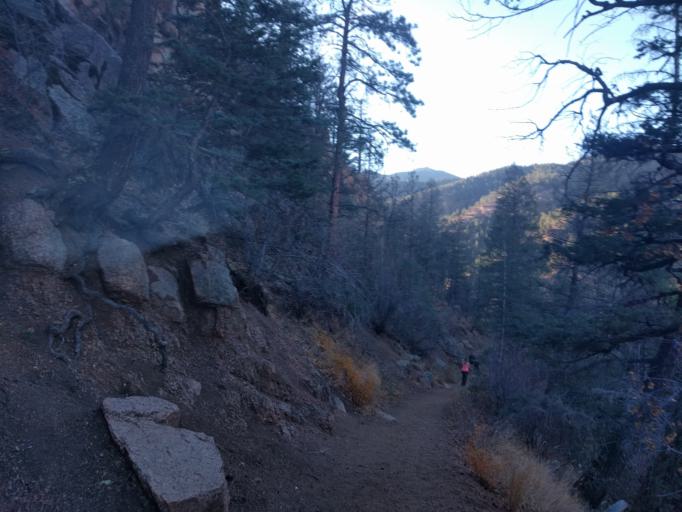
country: US
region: Colorado
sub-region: El Paso County
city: Colorado Springs
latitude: 38.7905
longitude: -104.8819
